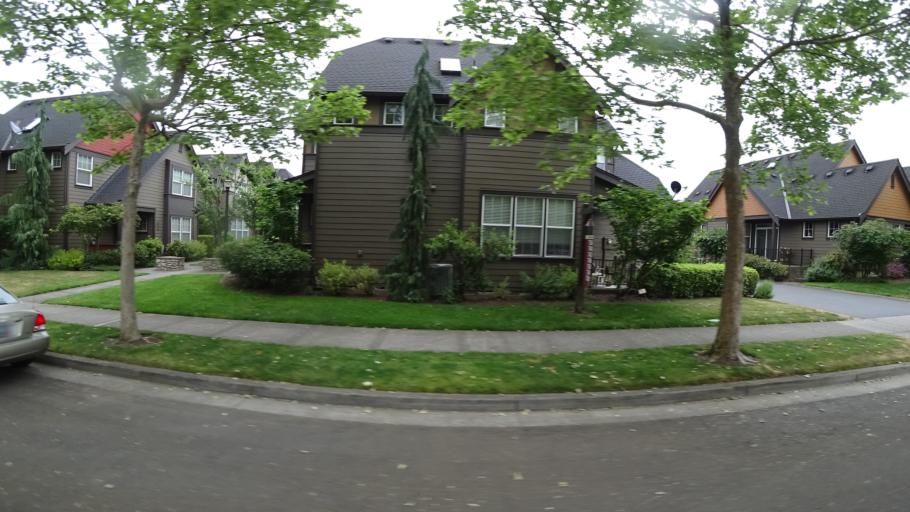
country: US
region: Oregon
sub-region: Washington County
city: Rockcreek
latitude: 45.5295
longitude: -122.9051
